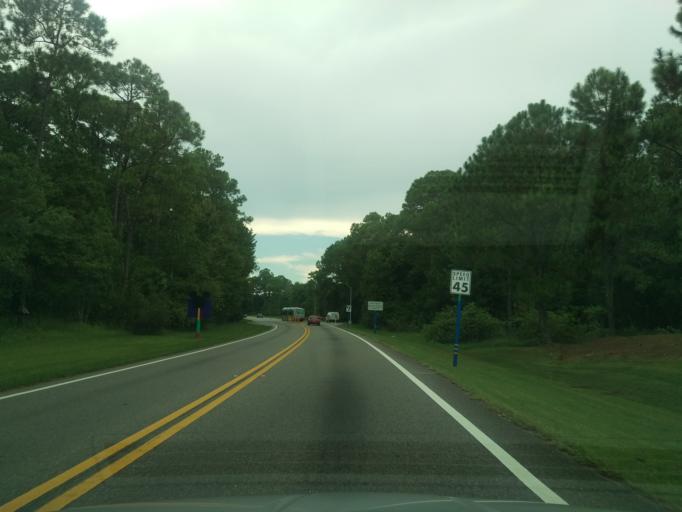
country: US
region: Florida
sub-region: Osceola County
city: Celebration
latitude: 28.3945
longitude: -81.5487
